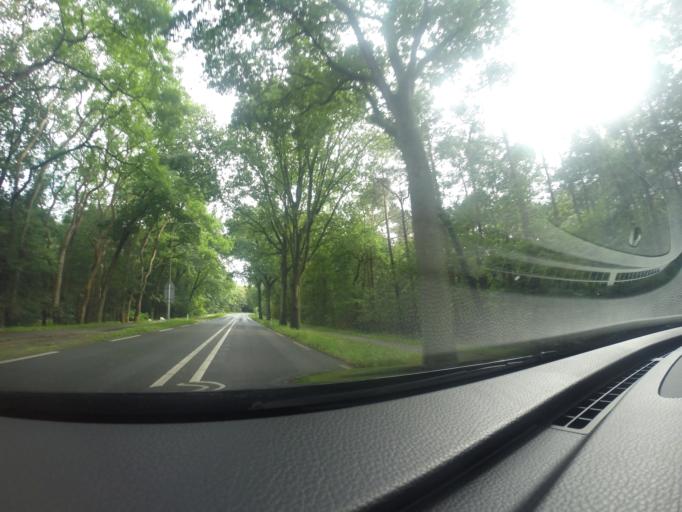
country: NL
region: Overijssel
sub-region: Gemeente Hof van Twente
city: Markelo
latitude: 52.2937
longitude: 6.5302
